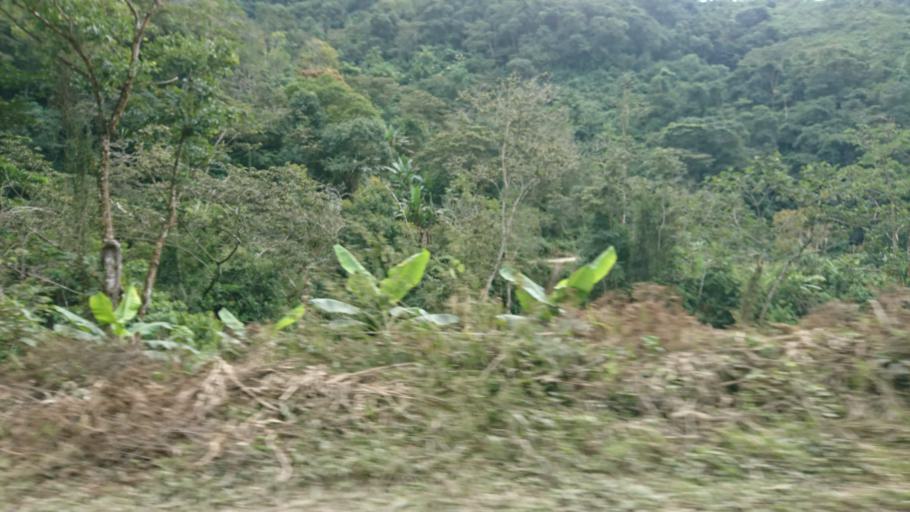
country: BO
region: La Paz
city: Coroico
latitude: -16.1145
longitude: -67.7900
